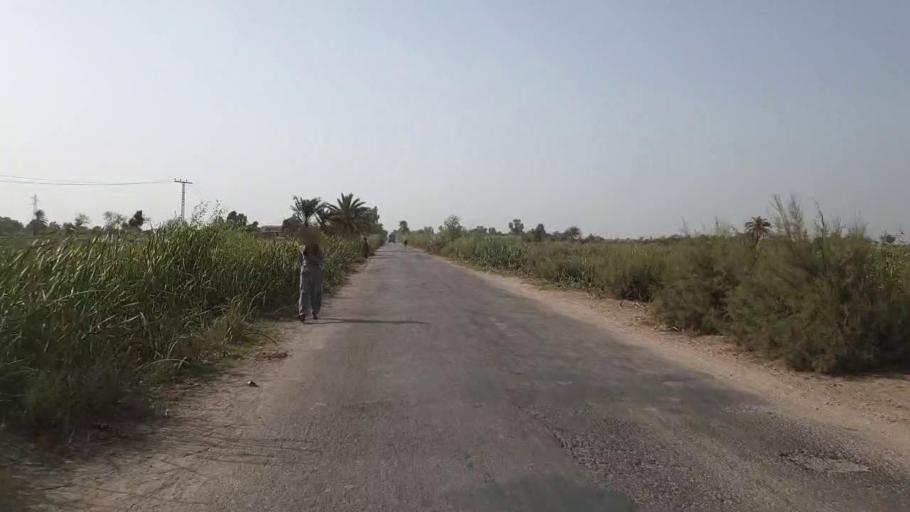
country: PK
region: Sindh
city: Khadro
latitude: 26.3316
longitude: 68.9295
